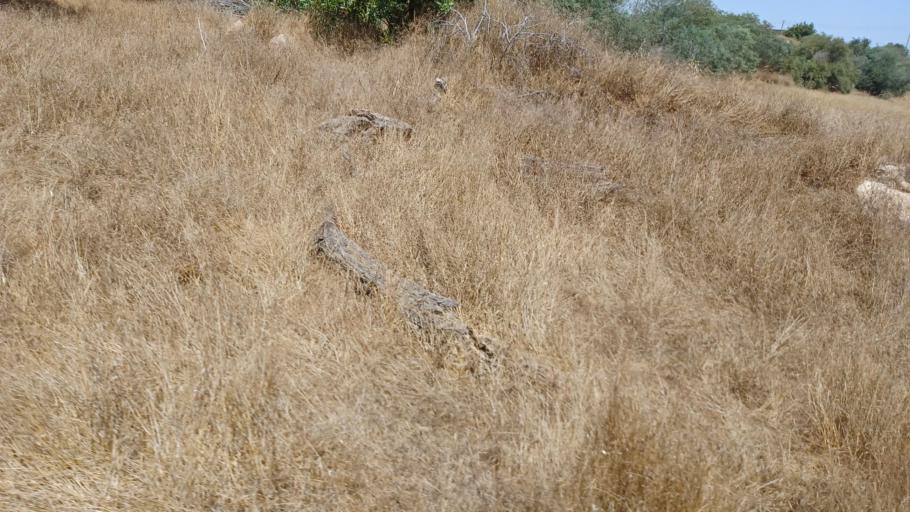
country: CY
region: Ammochostos
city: Frenaros
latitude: 35.0078
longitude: 33.9444
